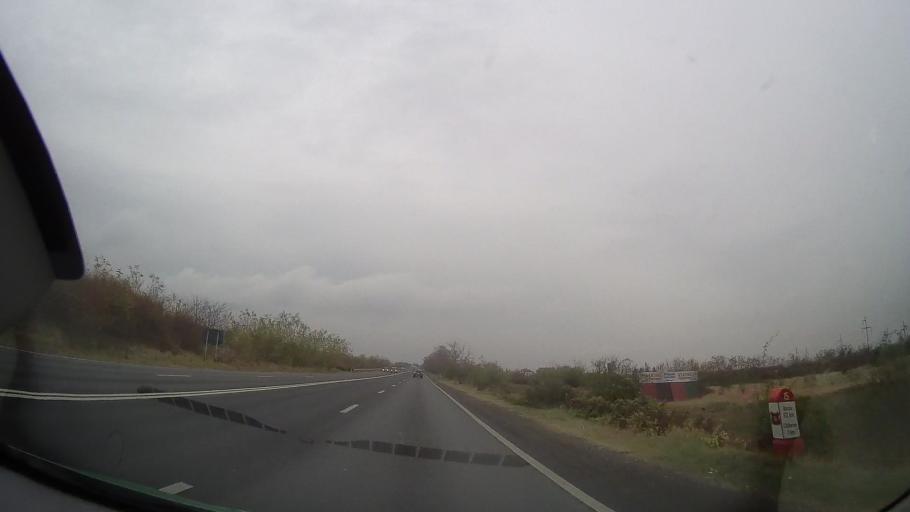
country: RO
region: Prahova
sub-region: Comuna Bucov
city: Chitorani
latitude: 44.9712
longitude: 26.1061
